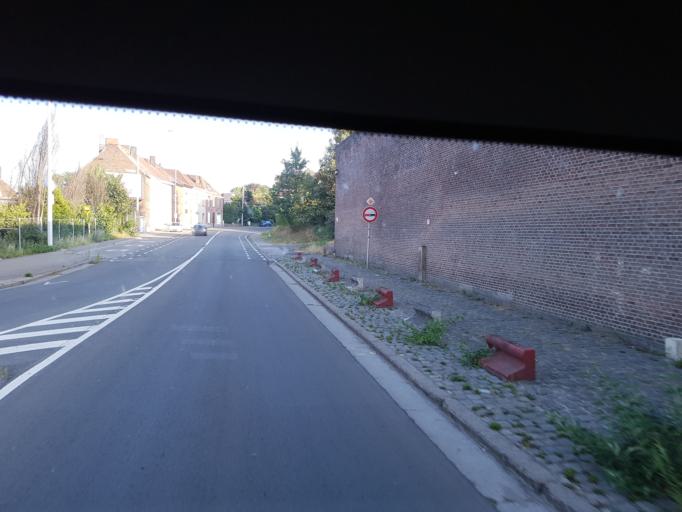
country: BE
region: Wallonia
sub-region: Province du Hainaut
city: Tournai
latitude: 50.5992
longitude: 3.4007
